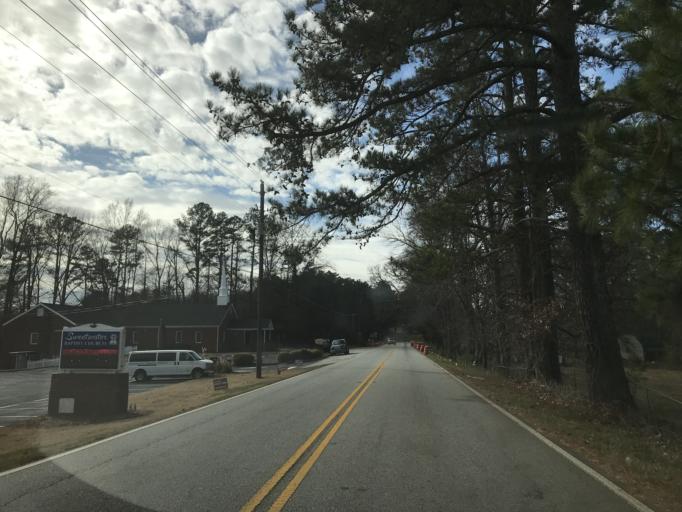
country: US
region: Georgia
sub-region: Douglas County
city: Douglasville
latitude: 33.7821
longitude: -84.7899
